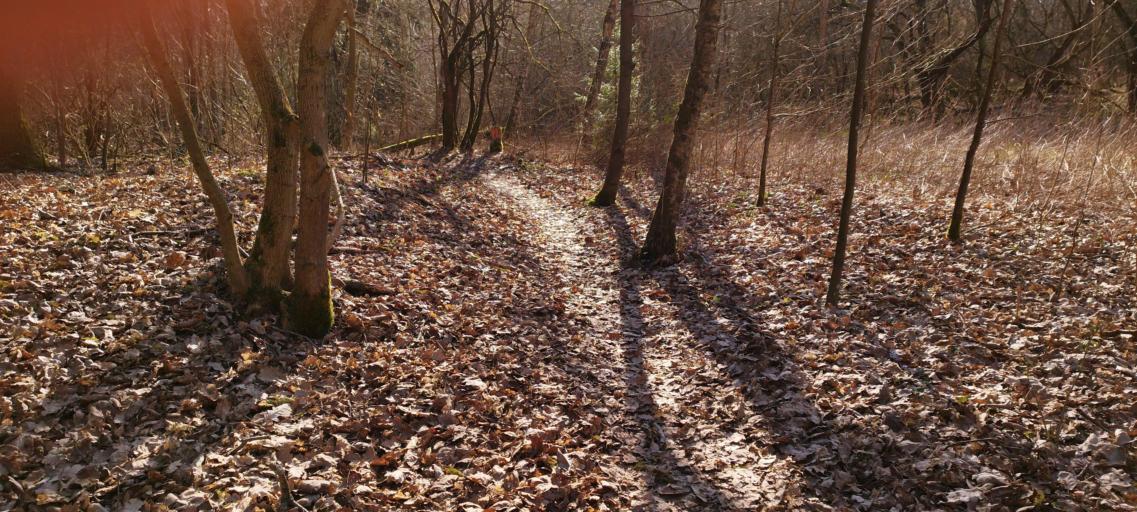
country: DE
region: Brandenburg
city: Grunheide
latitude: 52.4338
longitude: 13.8489
